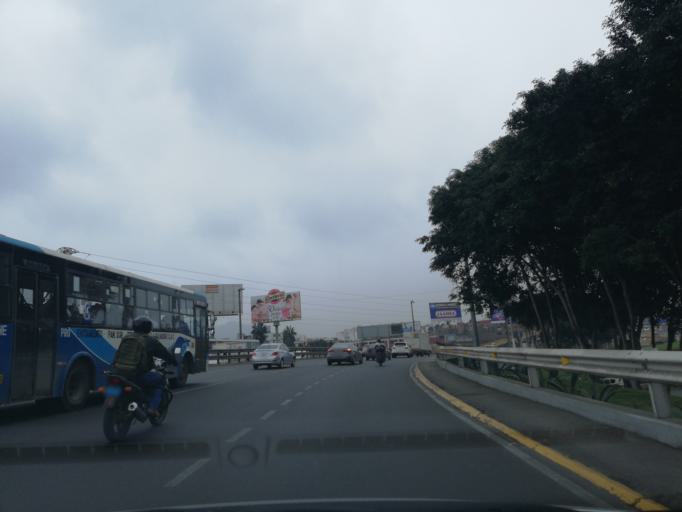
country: PE
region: Lima
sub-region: Lima
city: San Luis
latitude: -12.0855
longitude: -76.9821
